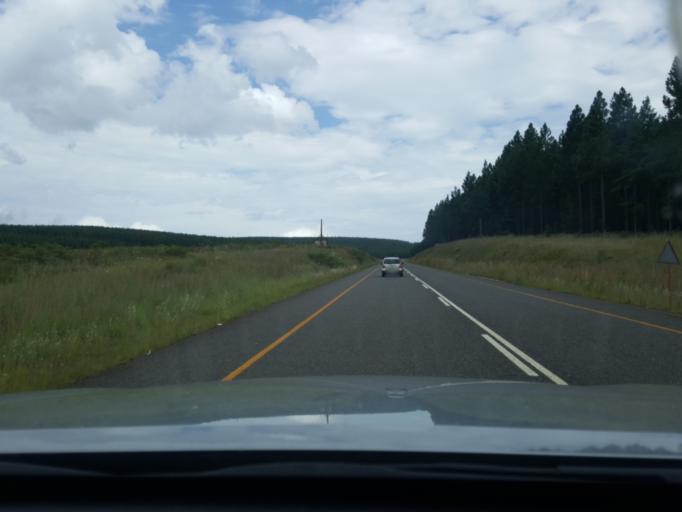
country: ZA
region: Mpumalanga
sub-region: Ehlanzeni District
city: Graksop
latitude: -25.1550
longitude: 30.8329
